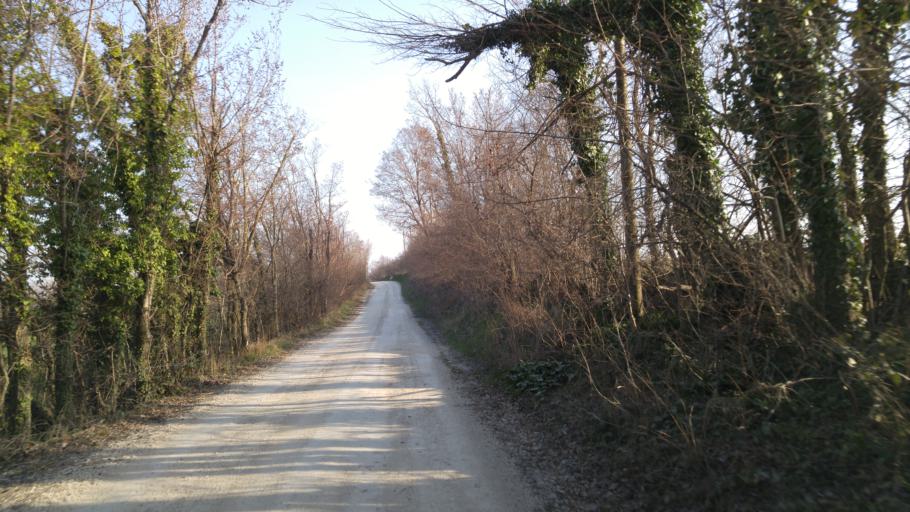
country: IT
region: The Marches
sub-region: Provincia di Pesaro e Urbino
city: Bellocchi
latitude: 43.7639
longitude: 12.9974
